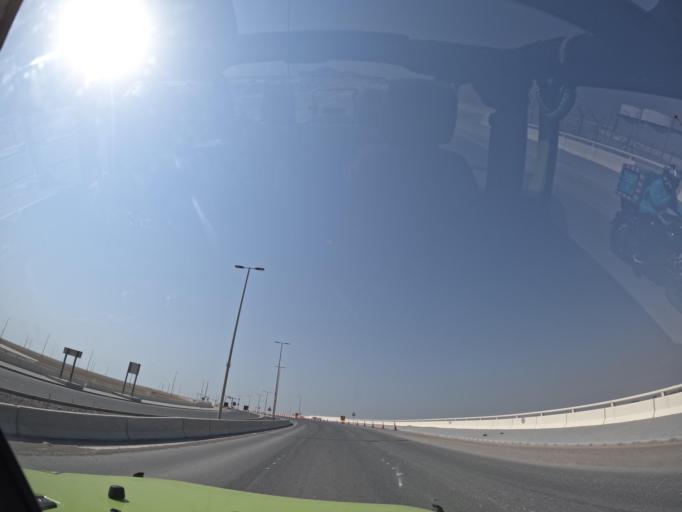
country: AE
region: Abu Dhabi
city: Abu Dhabi
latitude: 24.4632
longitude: 54.6315
